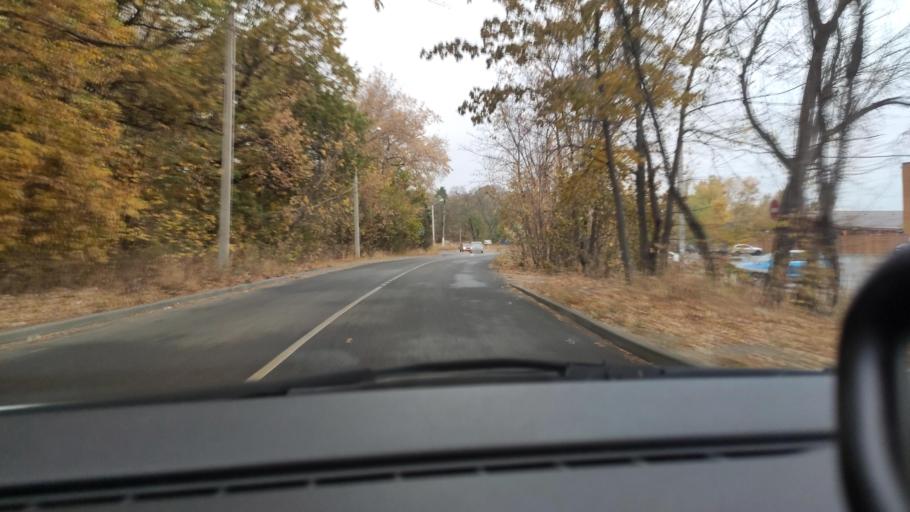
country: RU
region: Voronezj
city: Voronezh
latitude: 51.7246
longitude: 39.2351
